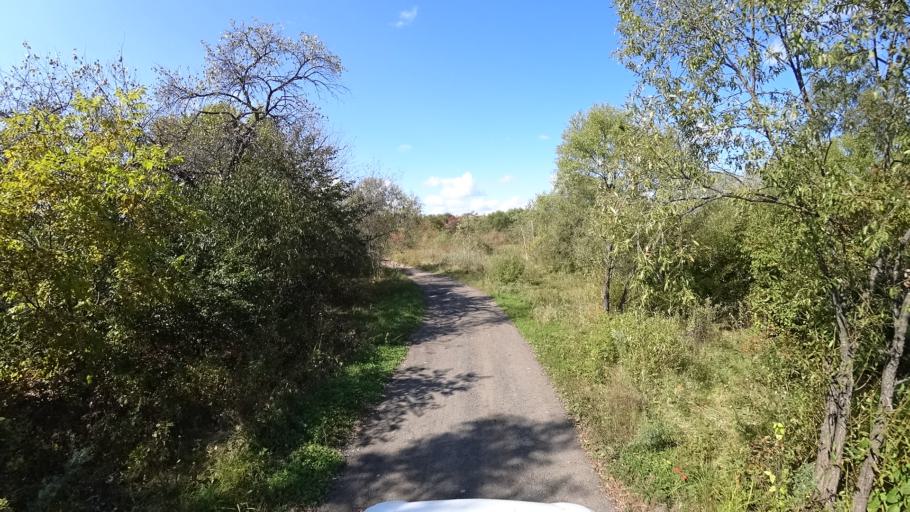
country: RU
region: Amur
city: Arkhara
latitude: 49.4002
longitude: 130.1289
